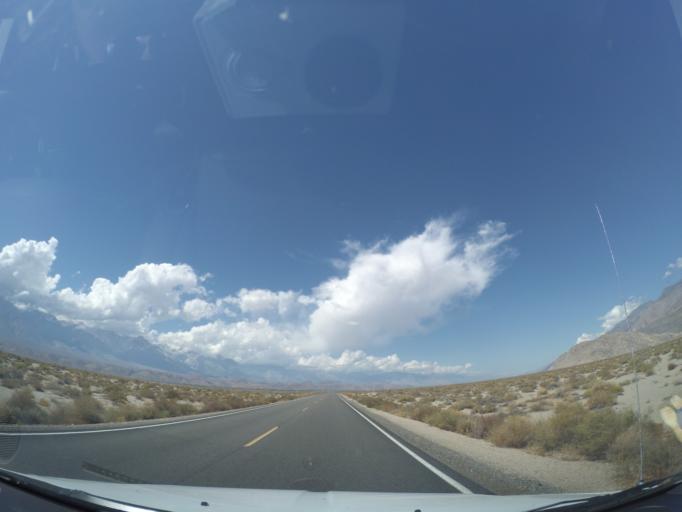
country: US
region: California
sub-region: Inyo County
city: Lone Pine
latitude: 36.5691
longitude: -117.9854
